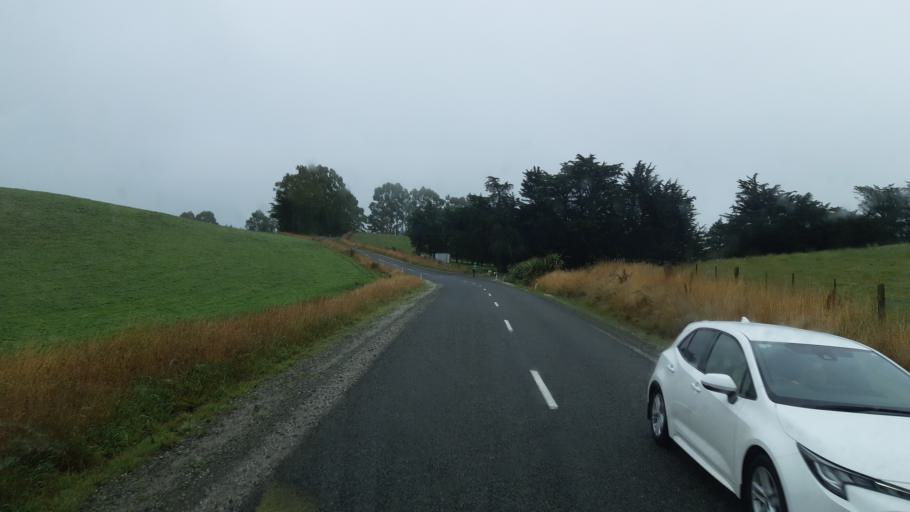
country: NZ
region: Otago
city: Oamaru
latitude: -44.9381
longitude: 170.7456
